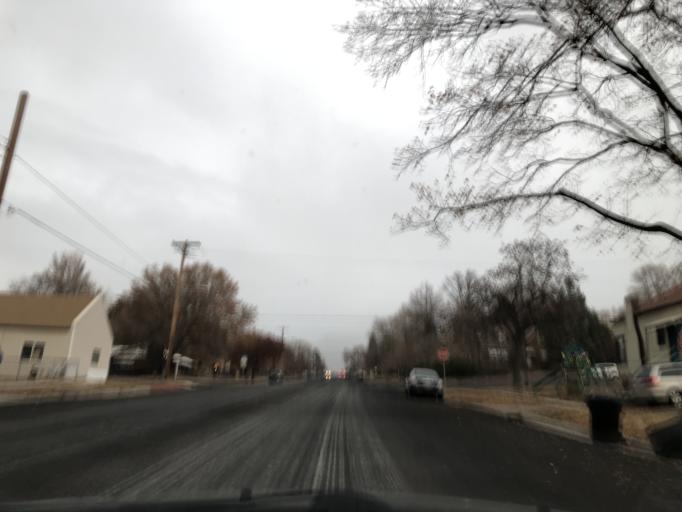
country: US
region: Utah
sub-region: Cache County
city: Logan
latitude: 41.7370
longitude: -111.8279
